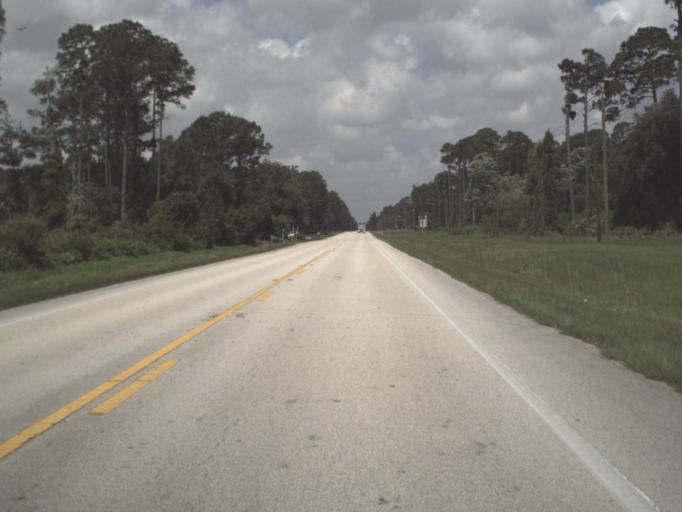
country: US
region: Florida
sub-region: Saint Johns County
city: Butler Beach
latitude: 29.7570
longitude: -81.2769
